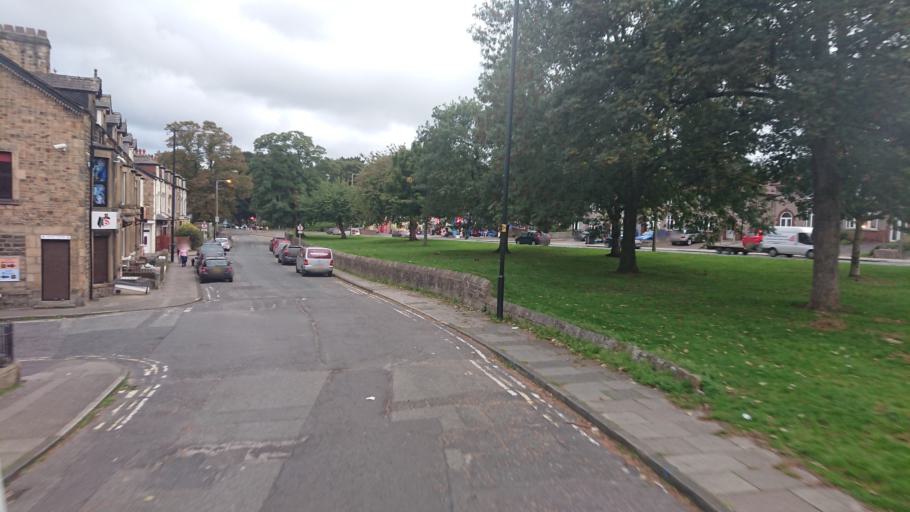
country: GB
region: England
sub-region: Lancashire
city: Lancaster
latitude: 54.0593
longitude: -2.8005
